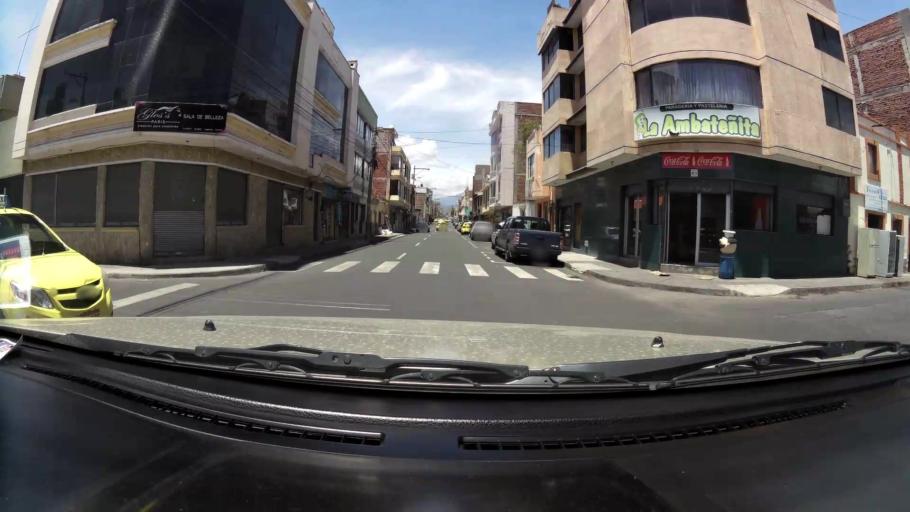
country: EC
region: Chimborazo
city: Riobamba
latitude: -1.6703
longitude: -78.6448
